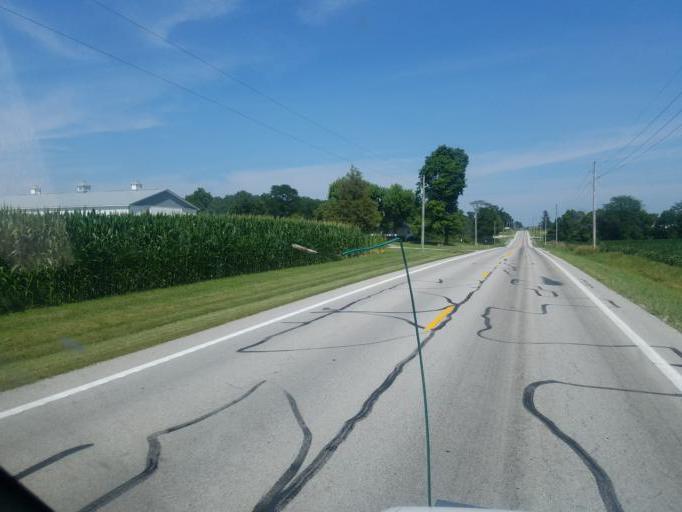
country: US
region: Ohio
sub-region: Auglaize County
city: Saint Marys
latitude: 40.4953
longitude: -84.3531
